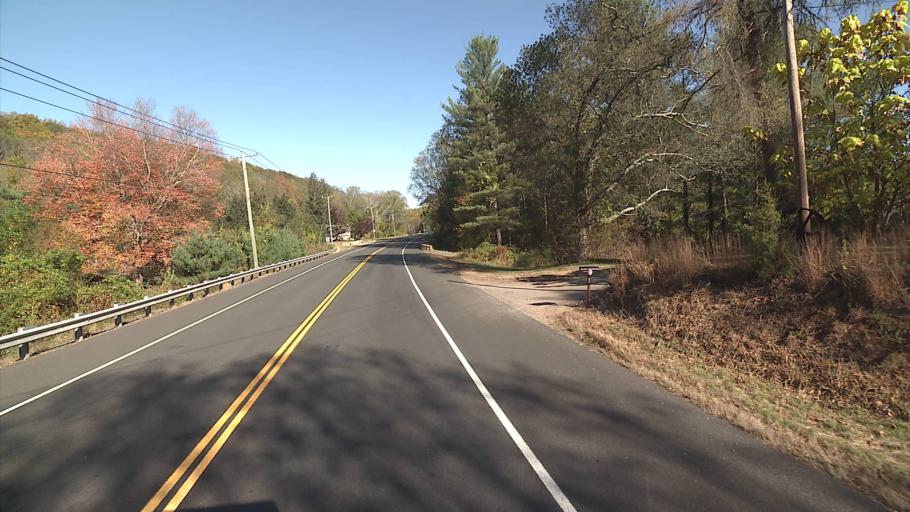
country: US
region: Connecticut
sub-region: Tolland County
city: Coventry Lake
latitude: 41.7645
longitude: -72.4058
